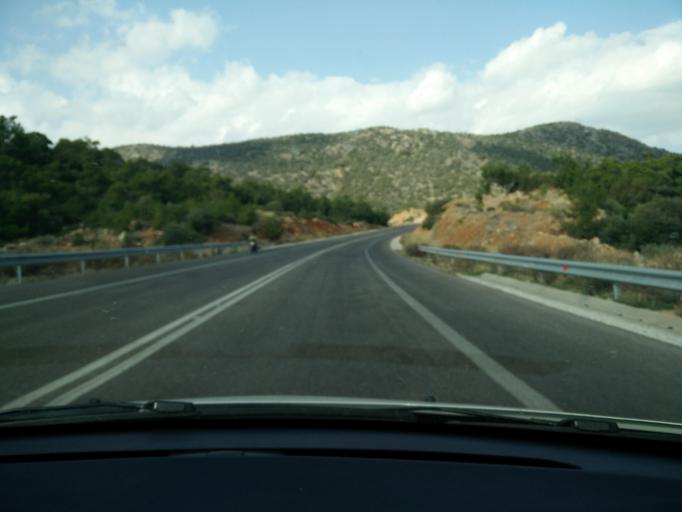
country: GR
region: Crete
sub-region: Nomos Lasithiou
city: Agios Nikolaos
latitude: 35.1425
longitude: 25.7073
